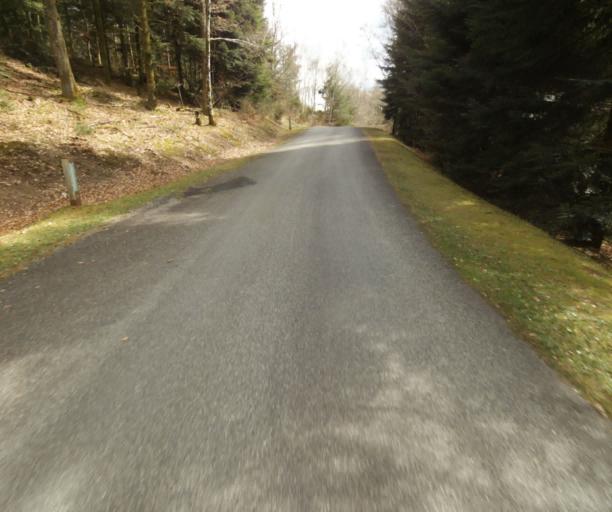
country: FR
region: Limousin
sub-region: Departement de la Correze
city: Correze
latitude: 45.2918
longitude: 1.9525
